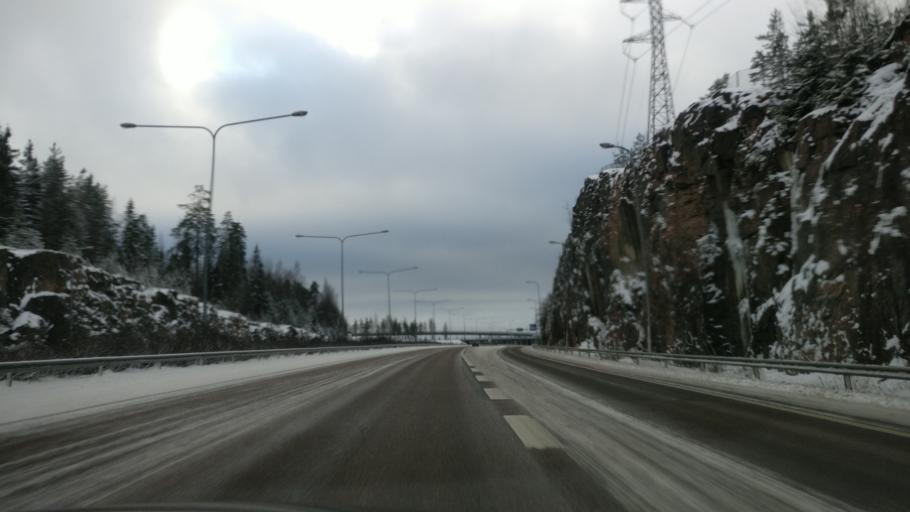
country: FI
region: Paijanne Tavastia
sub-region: Lahti
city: Lahti
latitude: 60.9746
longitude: 25.7269
